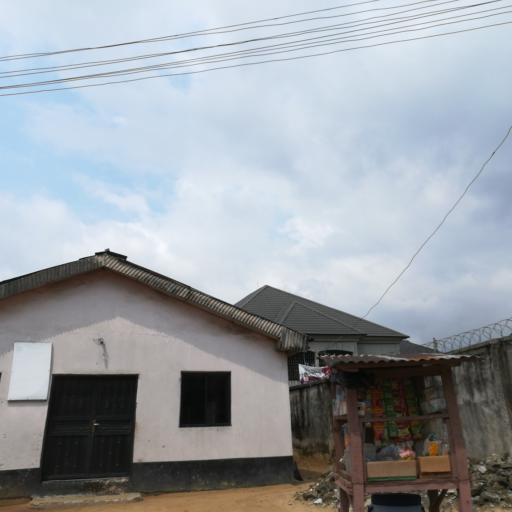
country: NG
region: Rivers
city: Port Harcourt
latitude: 4.8404
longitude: 7.0774
